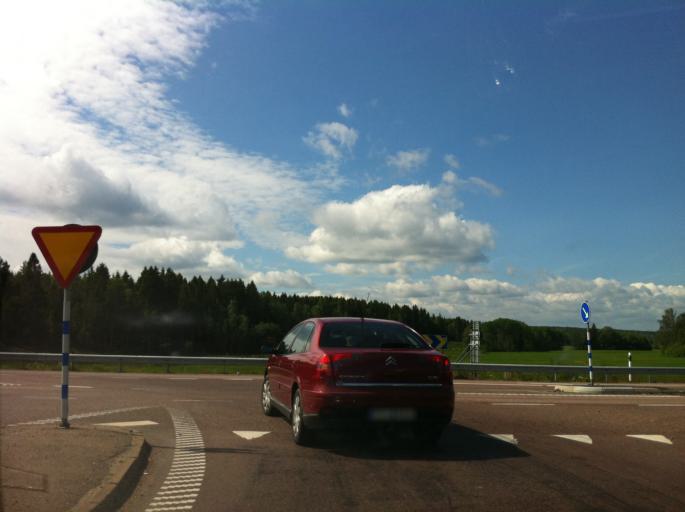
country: SE
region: Vaermland
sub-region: Karlstads Kommun
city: Valberg
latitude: 59.3725
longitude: 13.1398
